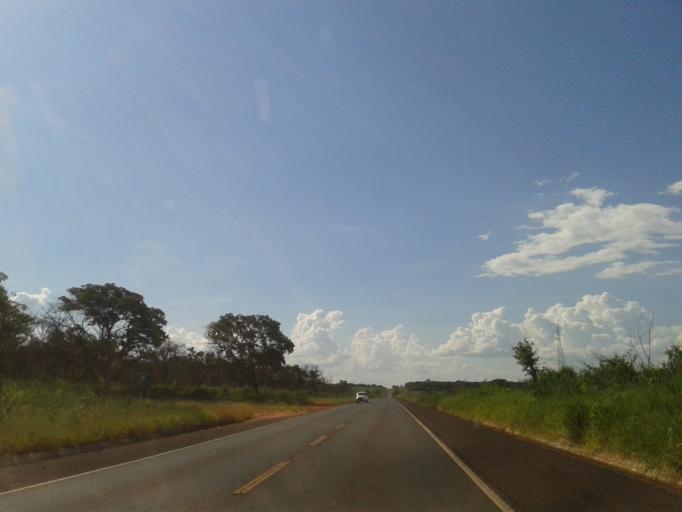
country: BR
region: Minas Gerais
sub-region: Santa Vitoria
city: Santa Vitoria
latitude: -19.0591
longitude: -50.3887
